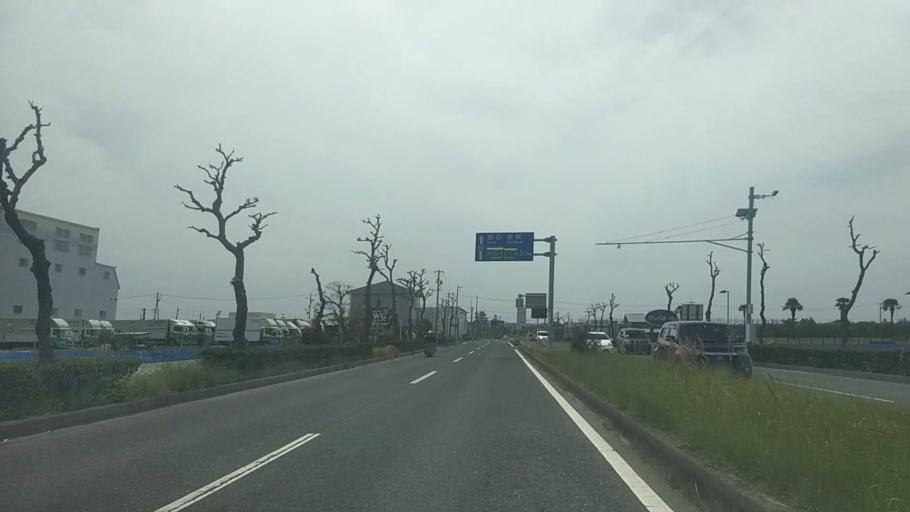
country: JP
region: Shizuoka
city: Hamamatsu
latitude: 34.6797
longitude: 137.6480
